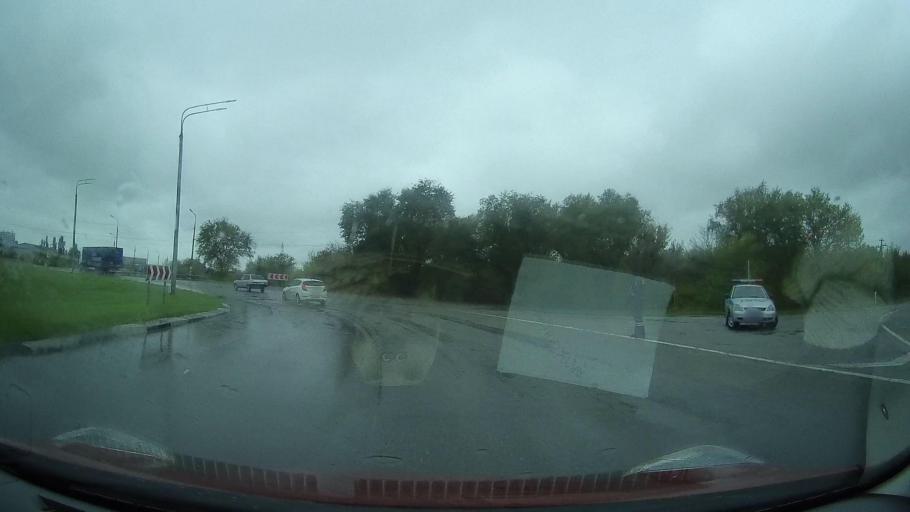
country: RU
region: Stavropol'skiy
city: Nevinnomyssk
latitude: 44.6424
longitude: 41.9604
